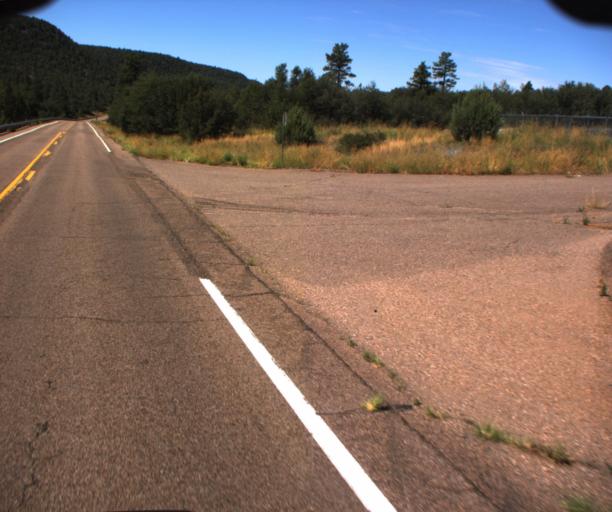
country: US
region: Arizona
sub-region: Navajo County
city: Cibecue
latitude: 33.9031
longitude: -110.3649
